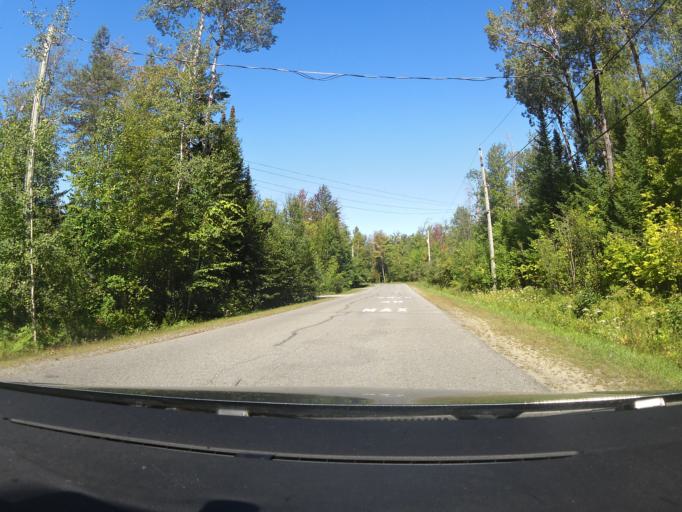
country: CA
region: Ontario
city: Bells Corners
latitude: 45.2503
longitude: -76.0040
